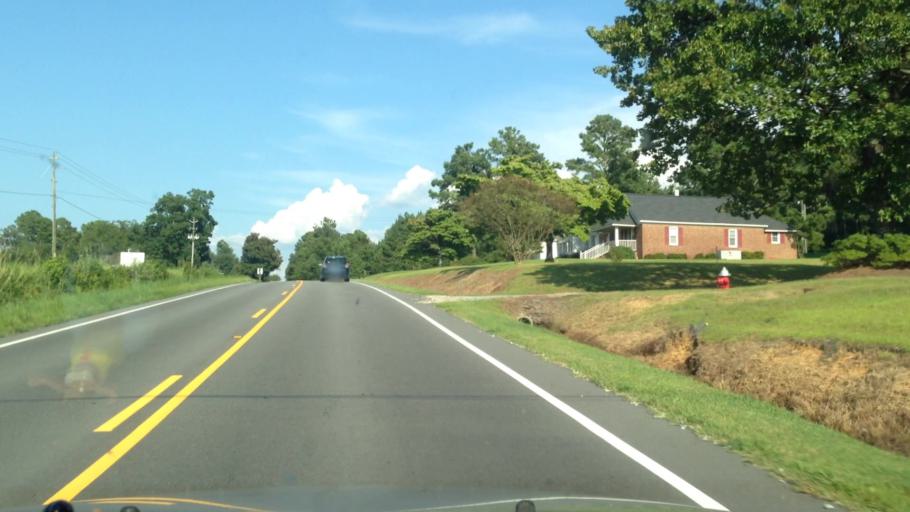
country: US
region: North Carolina
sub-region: Harnett County
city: Coats
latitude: 35.4119
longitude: -78.6829
